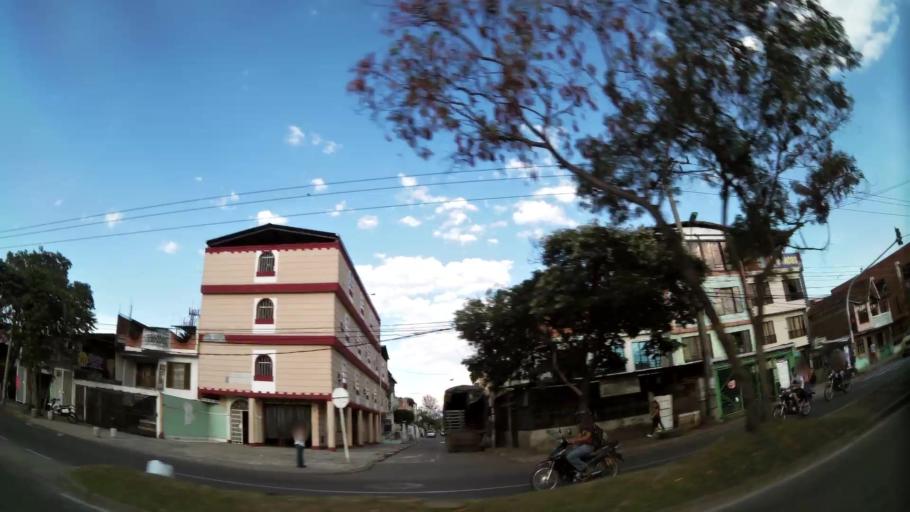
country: CO
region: Valle del Cauca
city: Cali
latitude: 3.4809
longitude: -76.4889
